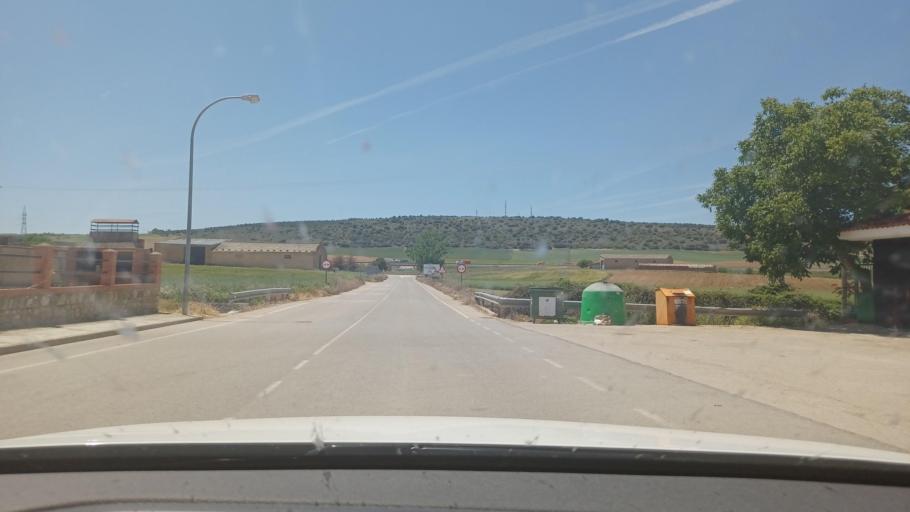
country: ES
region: Castille-La Mancha
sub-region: Provincia de Cuenca
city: Villares del Saz
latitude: 39.8383
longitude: -2.5060
